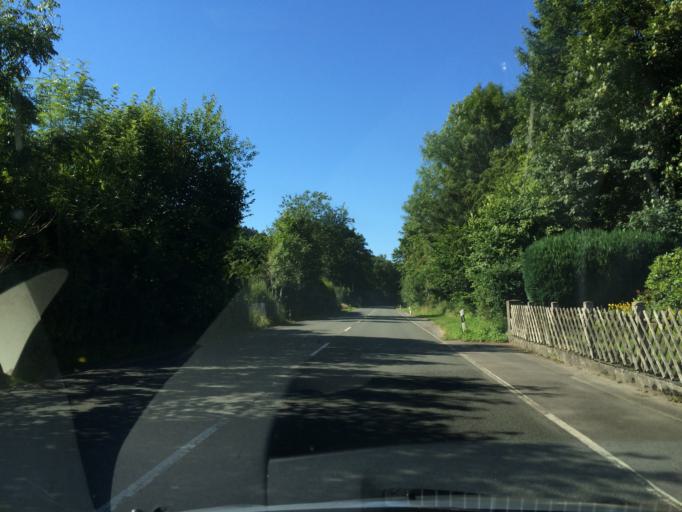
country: DE
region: North Rhine-Westphalia
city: Iserlohn
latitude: 51.3599
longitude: 7.7011
